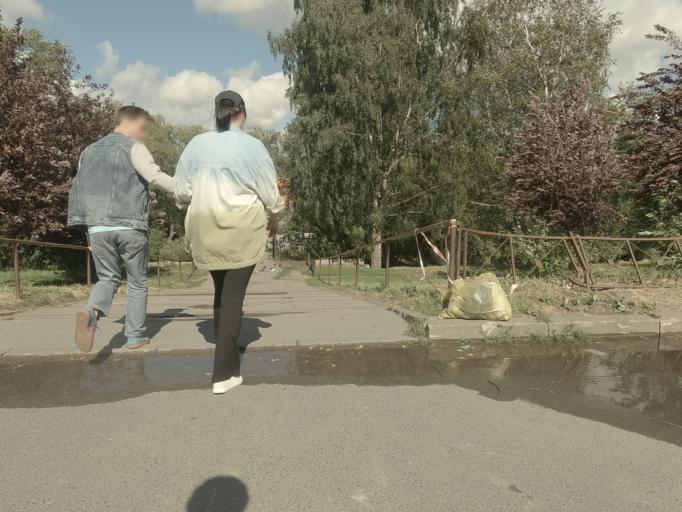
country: RU
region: St.-Petersburg
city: Krasnogvargeisky
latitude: 59.9296
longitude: 30.4292
